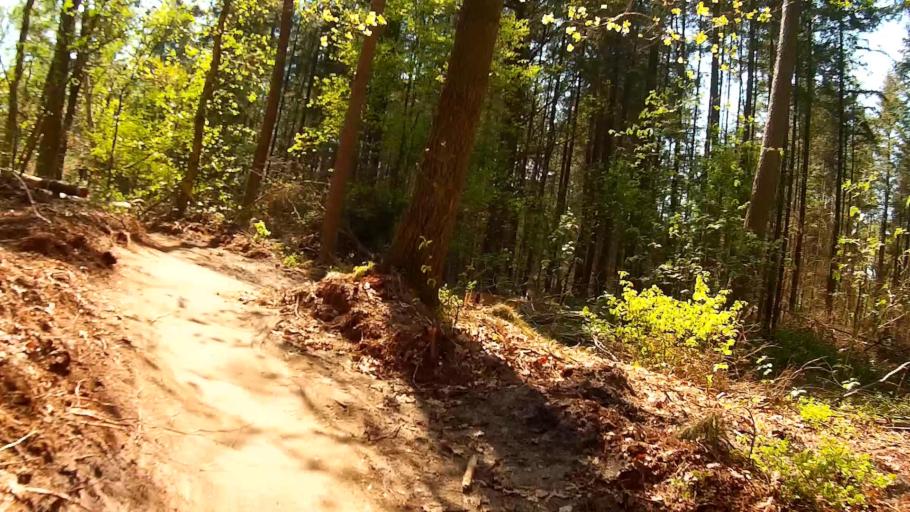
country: NL
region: Utrecht
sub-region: Gemeente Baarn
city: Baarn
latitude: 52.1893
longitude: 5.2373
